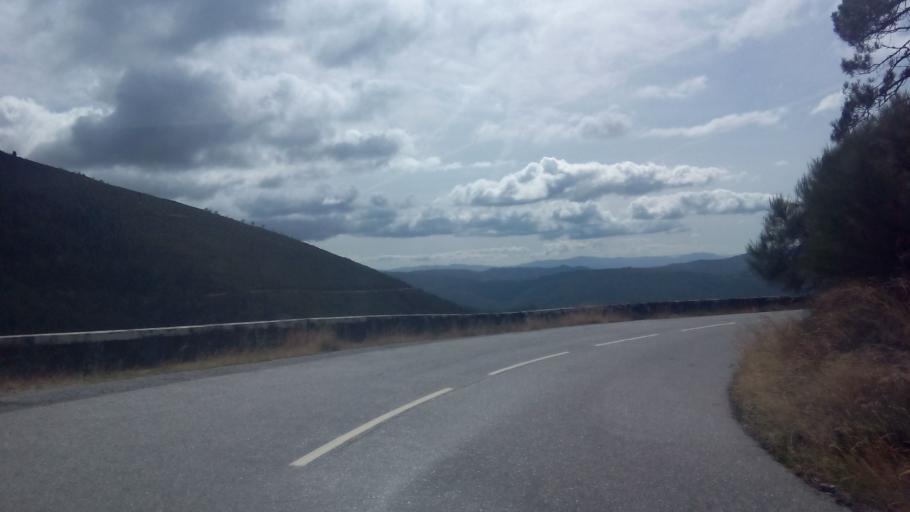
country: PT
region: Vila Real
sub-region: Mesao Frio
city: Mesao Frio
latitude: 41.2777
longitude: -7.9279
